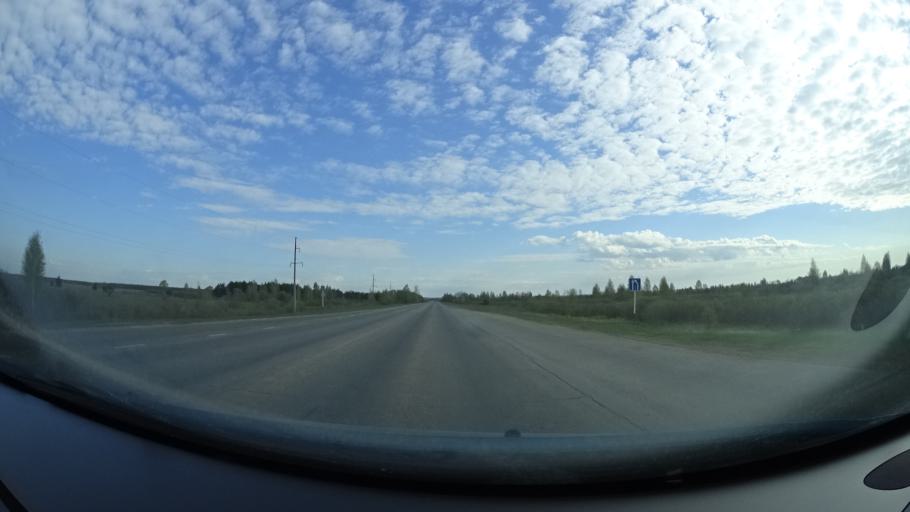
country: RU
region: Bashkortostan
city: Blagoveshchensk
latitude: 54.9919
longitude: 55.7758
